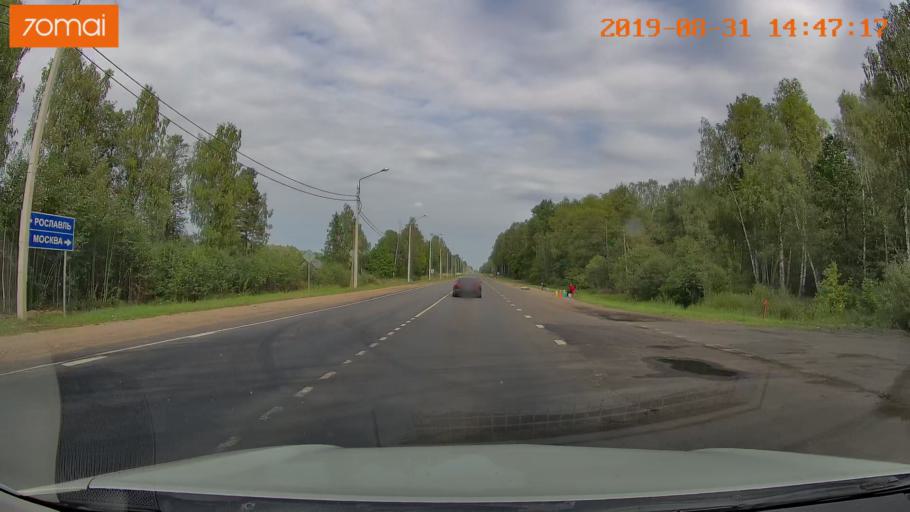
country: RU
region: Kaluga
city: Betlitsa
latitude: 54.2385
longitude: 33.7233
